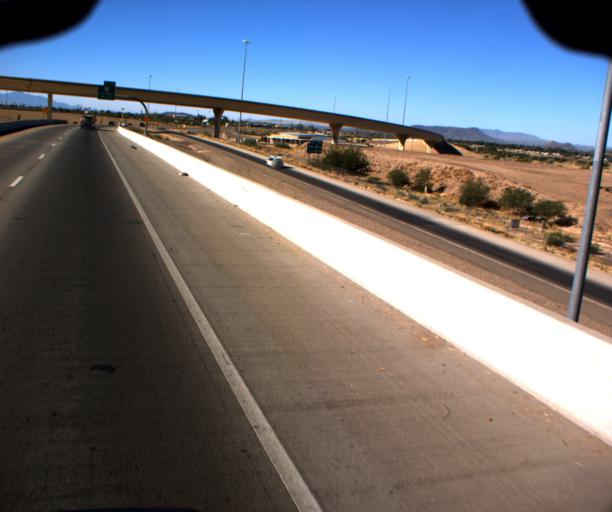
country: US
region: Arizona
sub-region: Pima County
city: South Tucson
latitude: 32.1976
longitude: -110.9793
